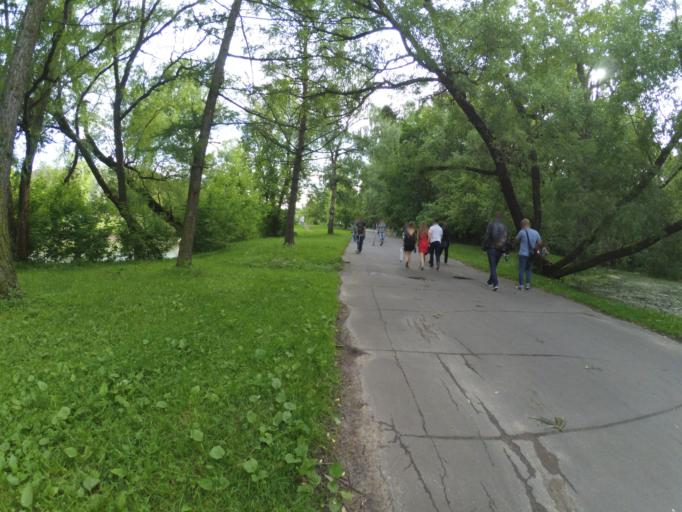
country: RU
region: Moscow
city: Ostankinskiy
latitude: 55.8347
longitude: 37.6096
